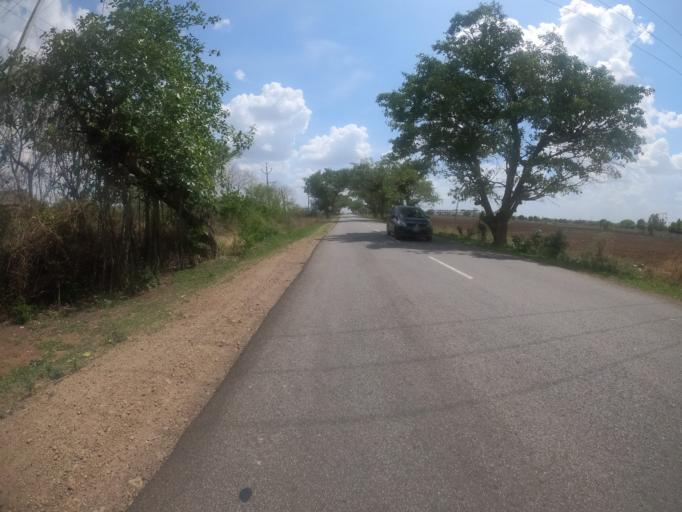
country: IN
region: Telangana
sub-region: Rangareddi
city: Sriramnagar
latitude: 17.3086
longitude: 78.1669
